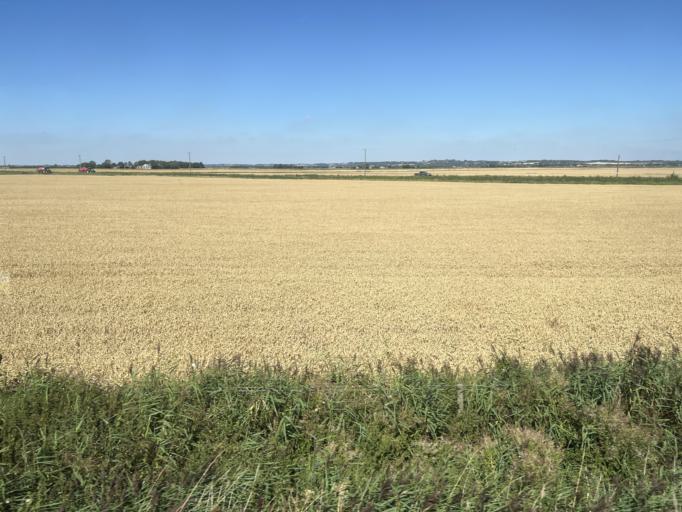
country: GB
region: England
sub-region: Lincolnshire
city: Spilsby
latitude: 53.1089
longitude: 0.1216
